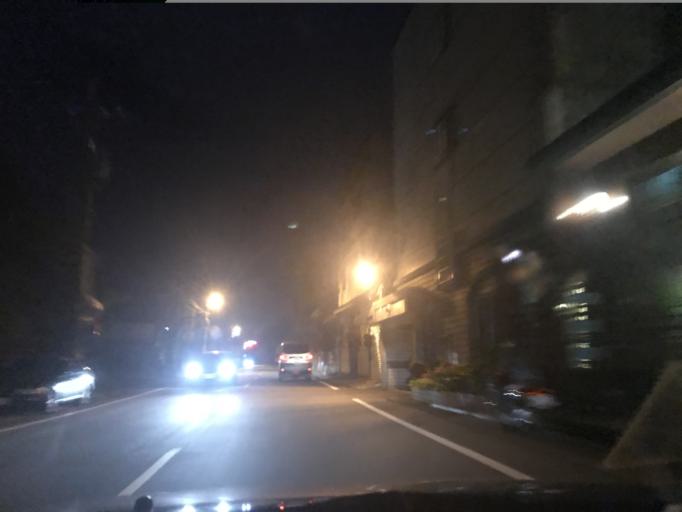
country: TW
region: Taiwan
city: Daxi
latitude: 24.9368
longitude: 121.2177
